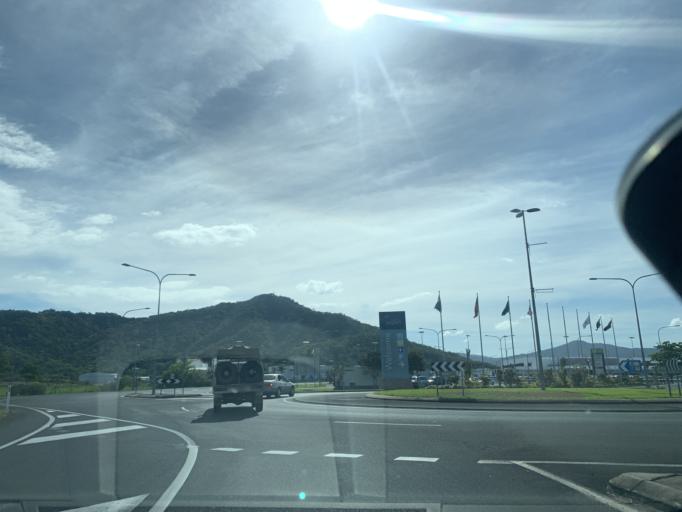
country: AU
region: Queensland
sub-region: Cairns
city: Cairns
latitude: -16.8790
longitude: 145.7575
